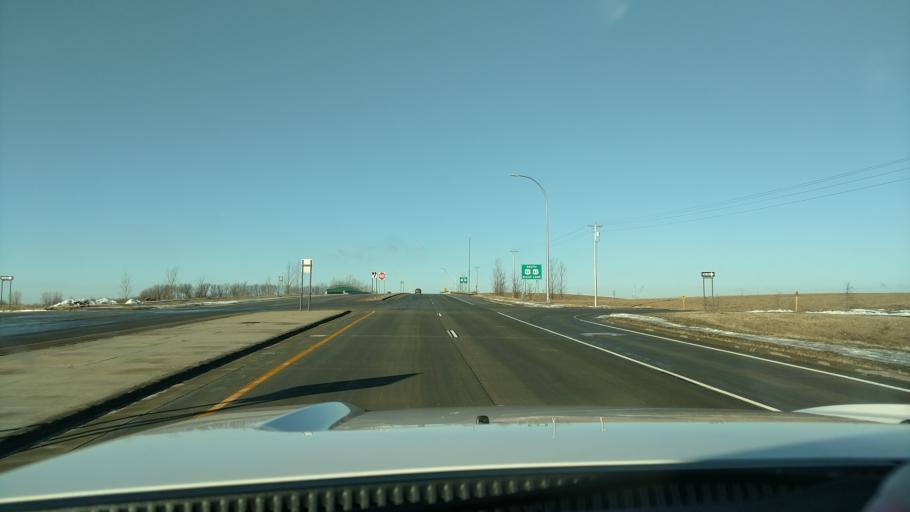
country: US
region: Minnesota
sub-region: Olmsted County
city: Oronoco
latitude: 44.1082
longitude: -92.5122
